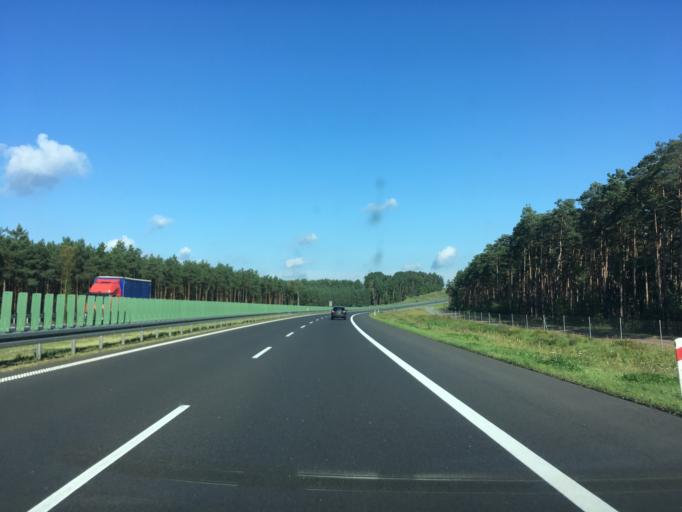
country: PL
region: Kujawsko-Pomorskie
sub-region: Powiat swiecki
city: Warlubie
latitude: 53.5239
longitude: 18.6002
